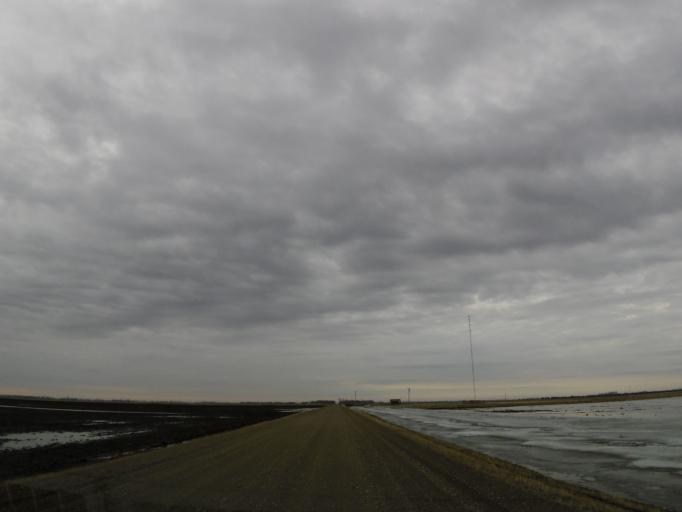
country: US
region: North Dakota
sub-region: Walsh County
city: Grafton
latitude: 48.4012
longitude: -97.4485
